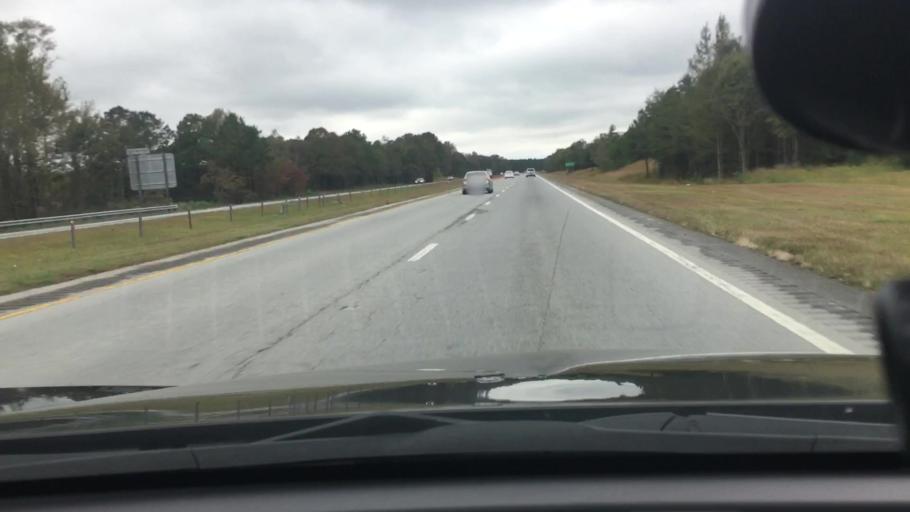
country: US
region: North Carolina
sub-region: Pitt County
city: Farmville
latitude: 35.6193
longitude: -77.6899
